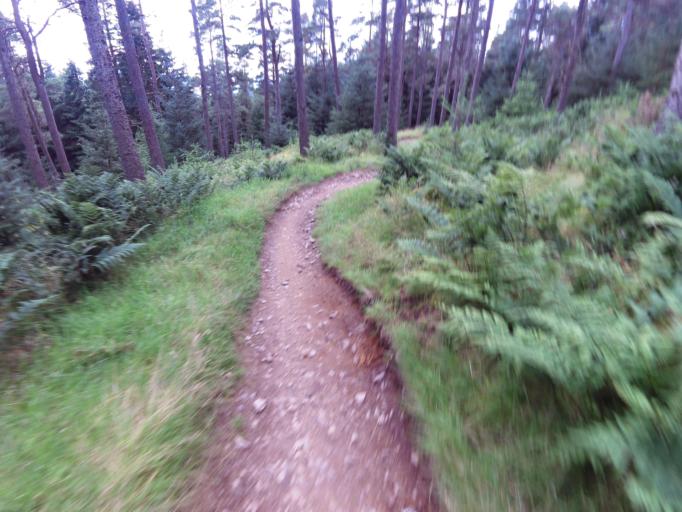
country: GB
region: Scotland
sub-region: The Scottish Borders
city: Peebles
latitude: 55.6649
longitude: -3.1308
